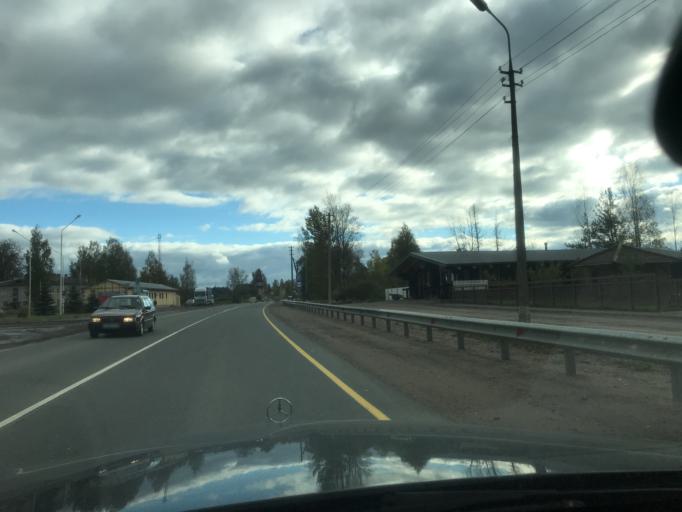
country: RU
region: Pskov
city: Opochka
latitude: 56.7098
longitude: 28.6911
